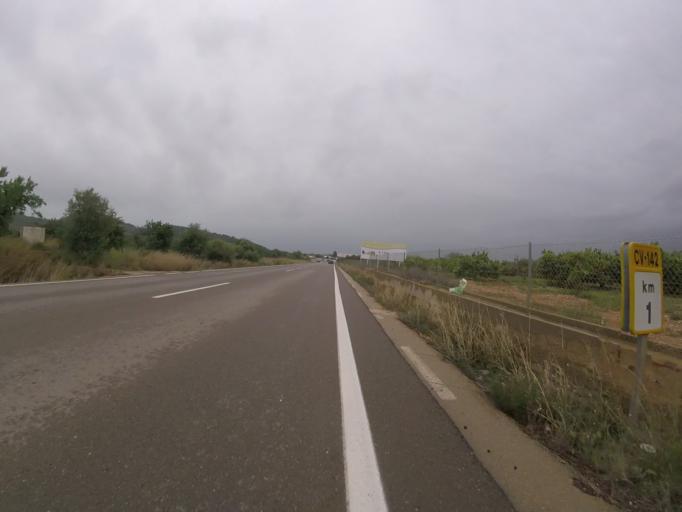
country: ES
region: Valencia
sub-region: Provincia de Castello
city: Alcoceber
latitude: 40.2590
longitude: 0.2440
